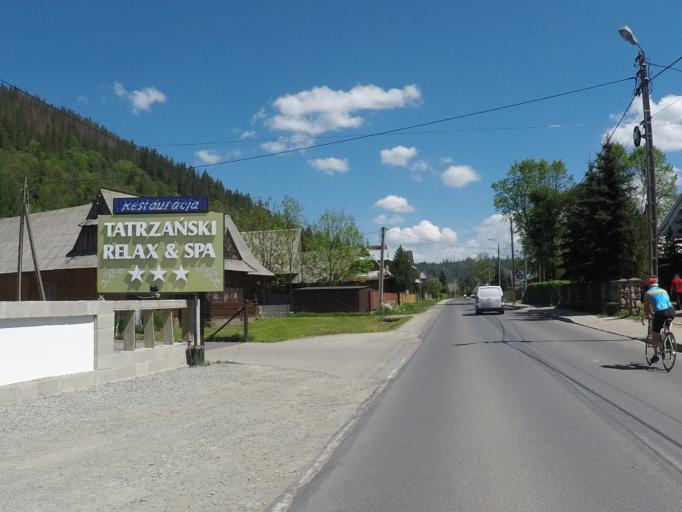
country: PL
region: Lesser Poland Voivodeship
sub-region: Powiat tatrzanski
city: Poronin
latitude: 49.3316
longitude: 20.0176
